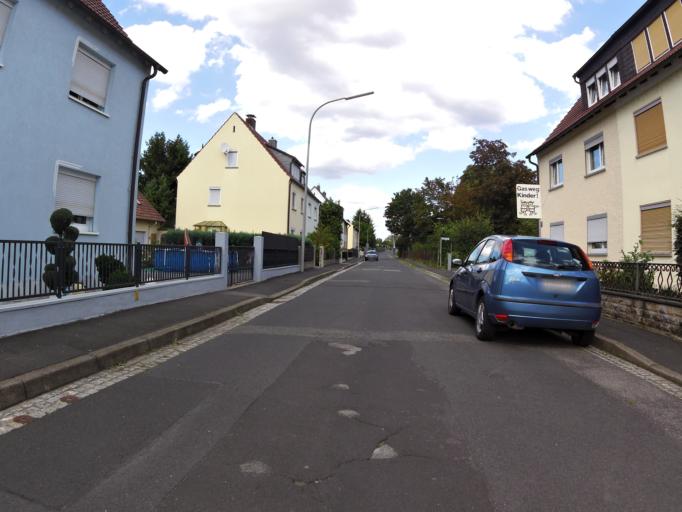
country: DE
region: Bavaria
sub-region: Regierungsbezirk Unterfranken
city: Bergrheinfeld
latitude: 50.0157
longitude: 10.1897
